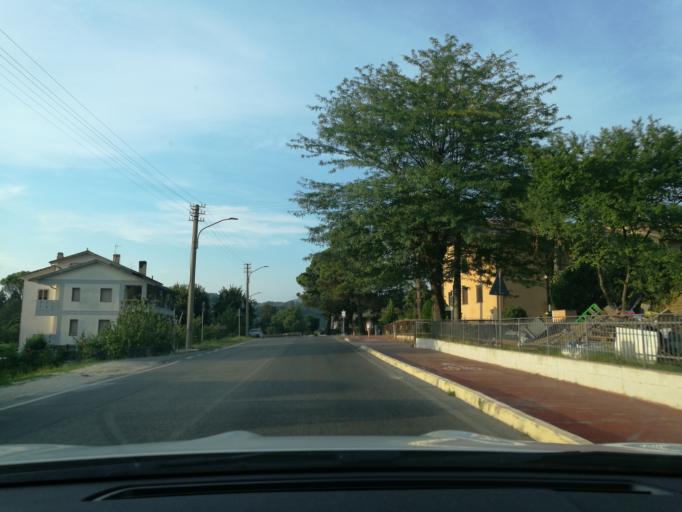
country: IT
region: Umbria
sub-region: Provincia di Terni
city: San Gemini
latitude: 42.6190
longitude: 12.5506
